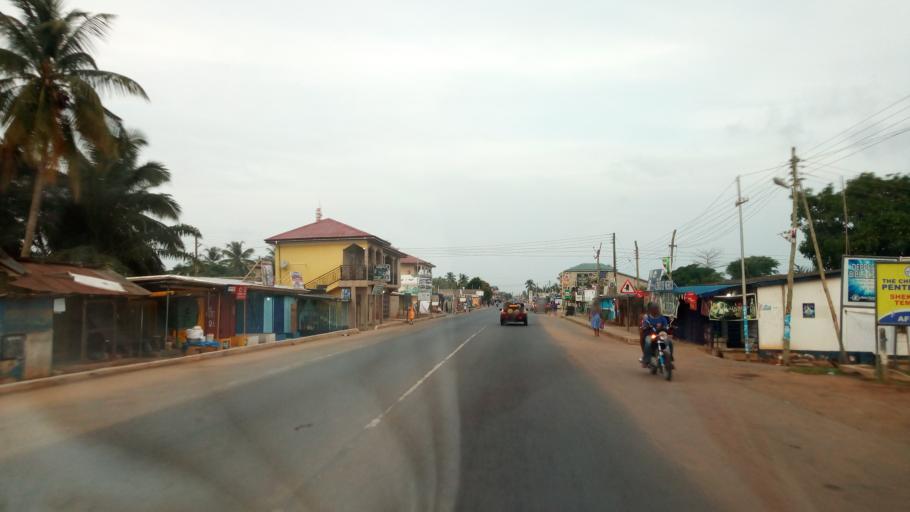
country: TG
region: Maritime
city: Lome
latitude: 6.1201
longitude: 1.1805
